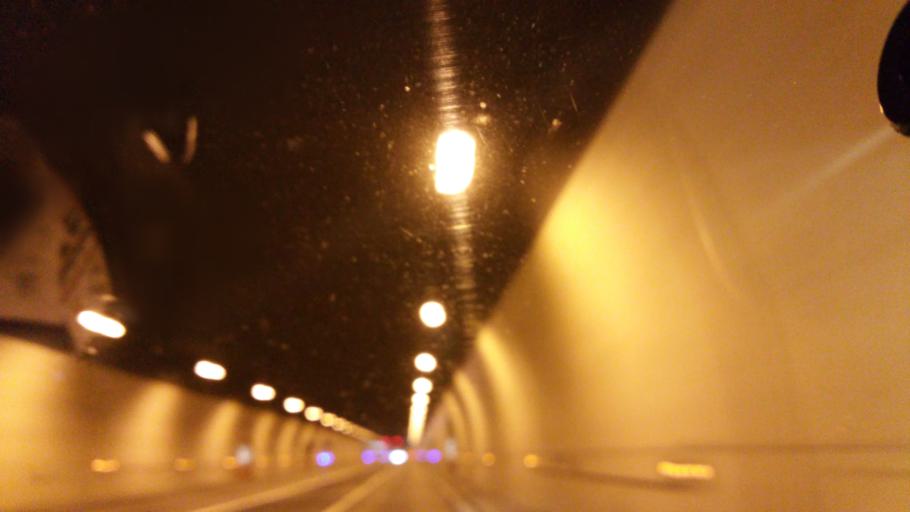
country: FR
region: Rhone-Alpes
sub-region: Departement de la Savoie
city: Saint-Michel-de-Maurienne
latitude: 45.2079
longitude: 6.5310
